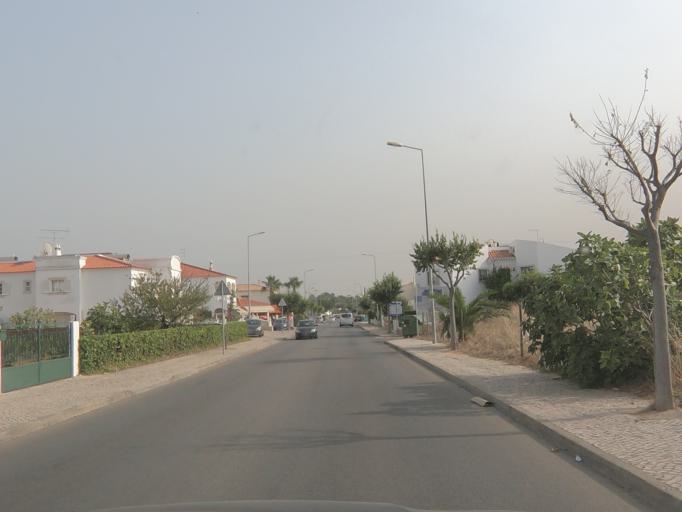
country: PT
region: Faro
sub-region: Albufeira
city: Guia
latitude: 37.0954
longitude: -8.3097
